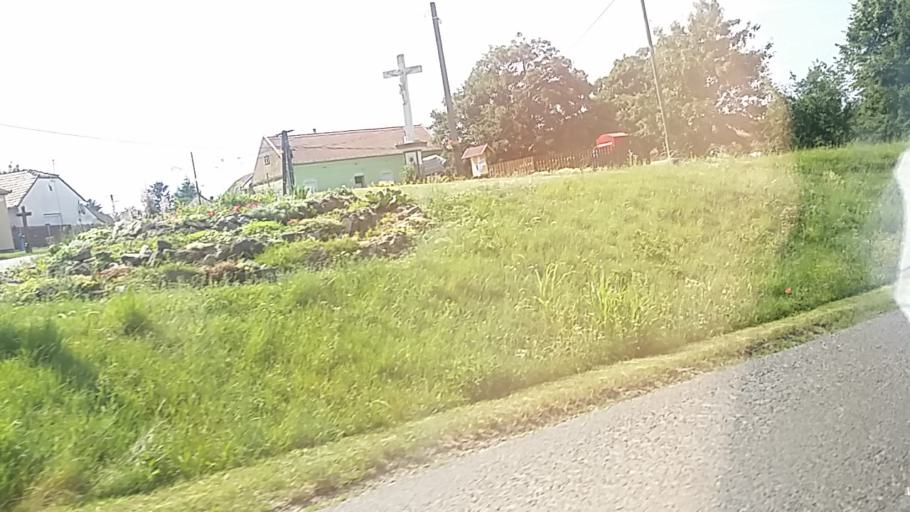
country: HU
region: Baranya
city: Siklos
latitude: 45.9096
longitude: 18.3364
